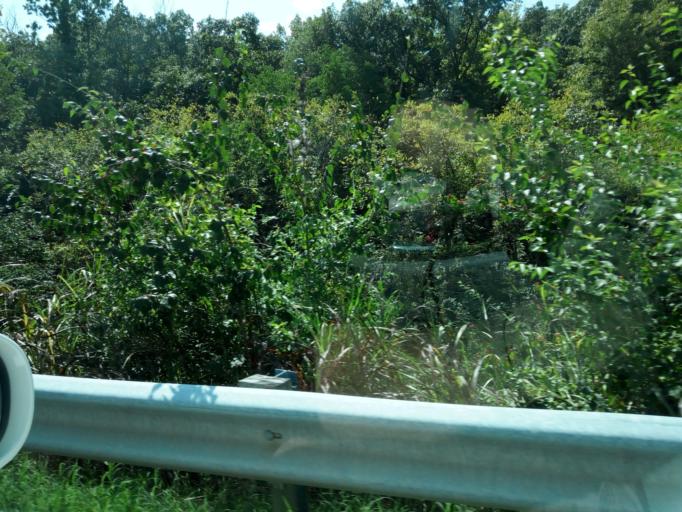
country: US
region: Kentucky
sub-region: Oldham County
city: Pewee Valley
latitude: 38.2407
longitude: -85.4603
